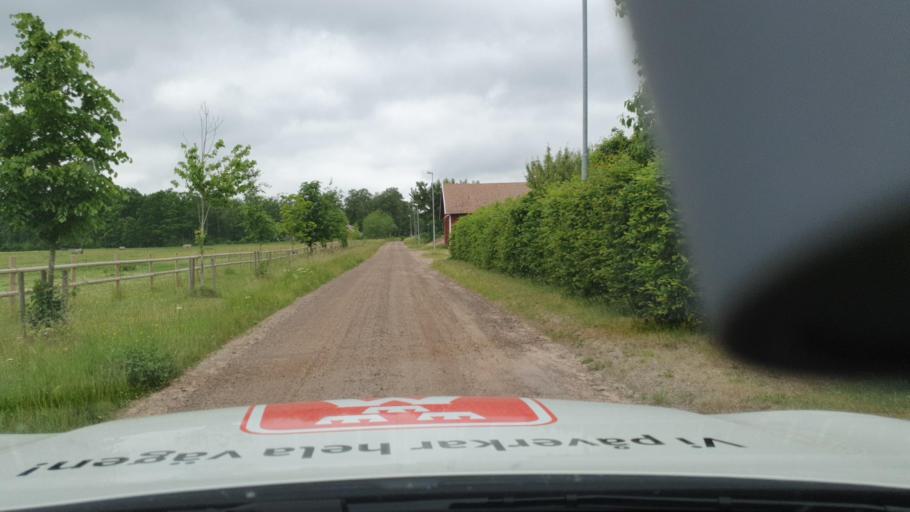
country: SE
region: Vaestra Goetaland
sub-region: Hjo Kommun
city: Hjo
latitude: 58.3522
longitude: 14.3461
